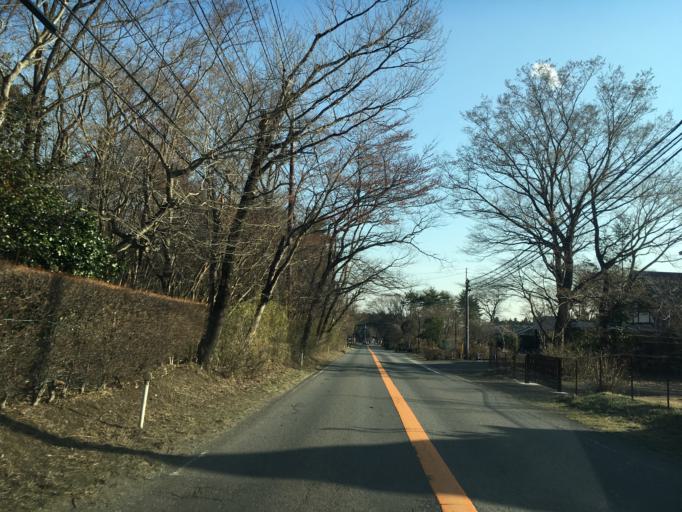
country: JP
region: Tochigi
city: Kuroiso
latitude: 37.0515
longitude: 140.0141
